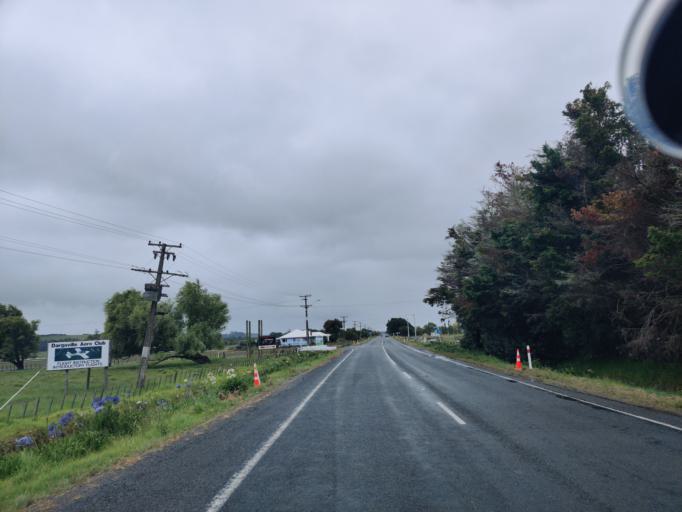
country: NZ
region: Northland
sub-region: Kaipara District
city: Dargaville
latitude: -35.9425
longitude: 173.8864
